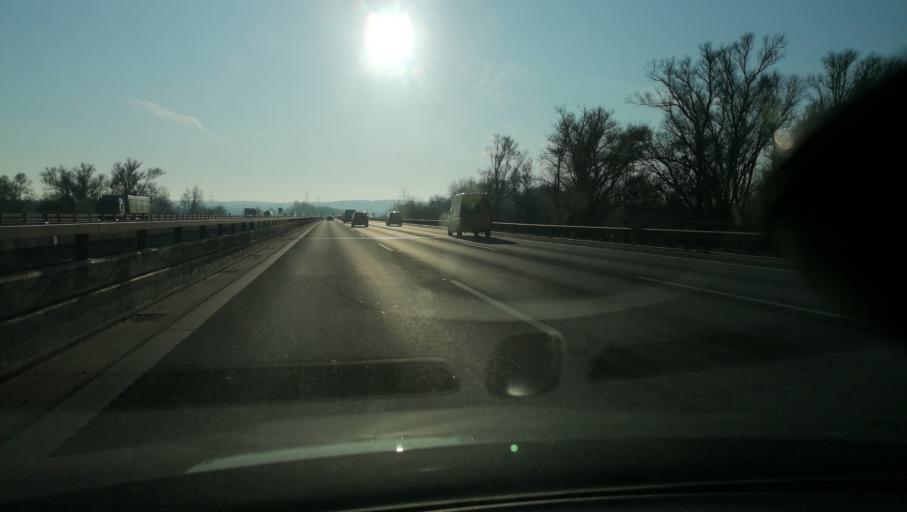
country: DE
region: Hamburg
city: Altona
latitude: 53.5013
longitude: 9.9126
